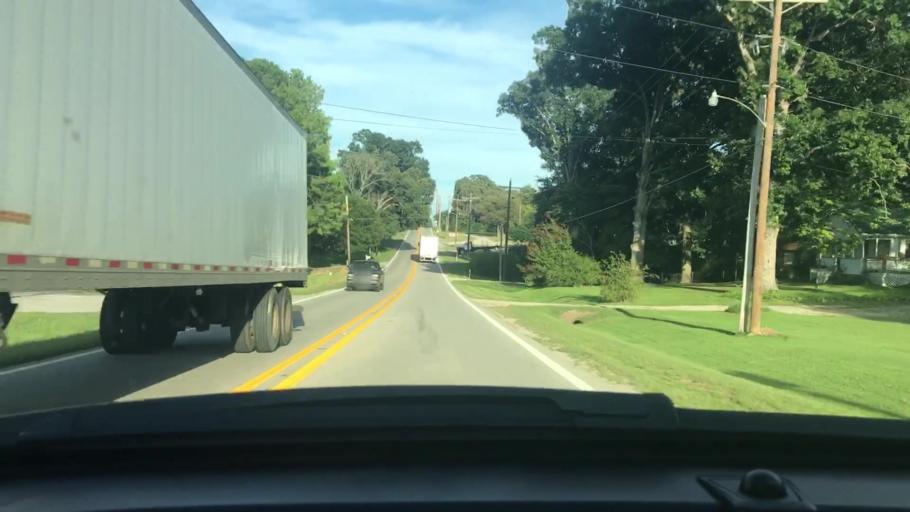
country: US
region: Arkansas
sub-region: Randolph County
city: Pocahontas
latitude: 36.2039
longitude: -91.1896
